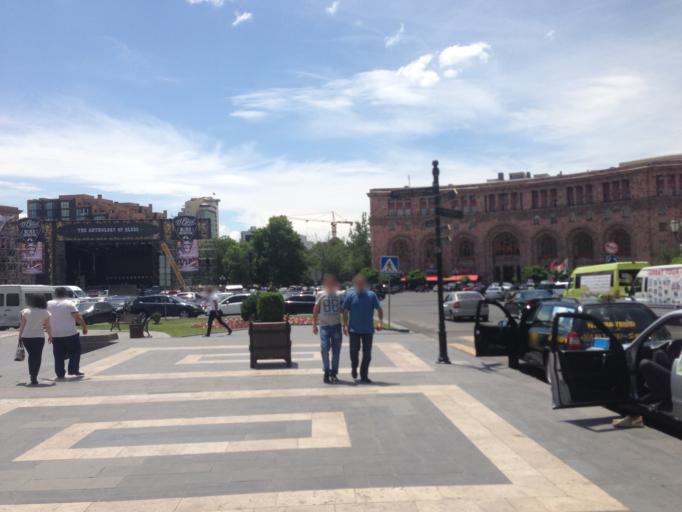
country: AM
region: Yerevan
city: Yerevan
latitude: 40.1786
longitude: 44.5130
